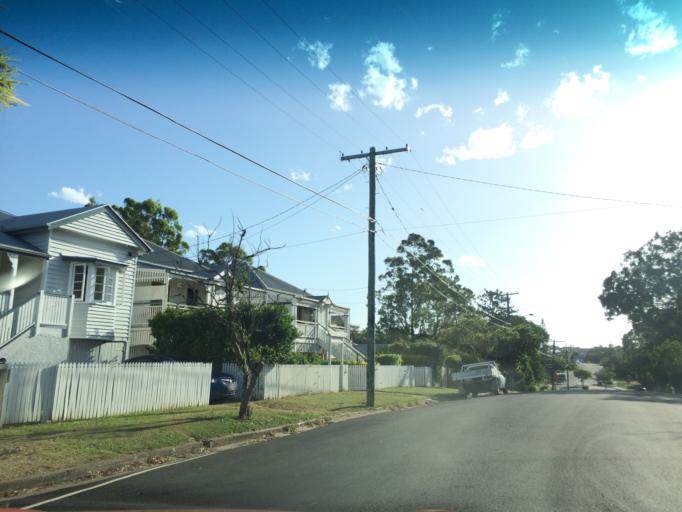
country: AU
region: Queensland
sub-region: Brisbane
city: Greenslopes
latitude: -27.4914
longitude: 153.0550
